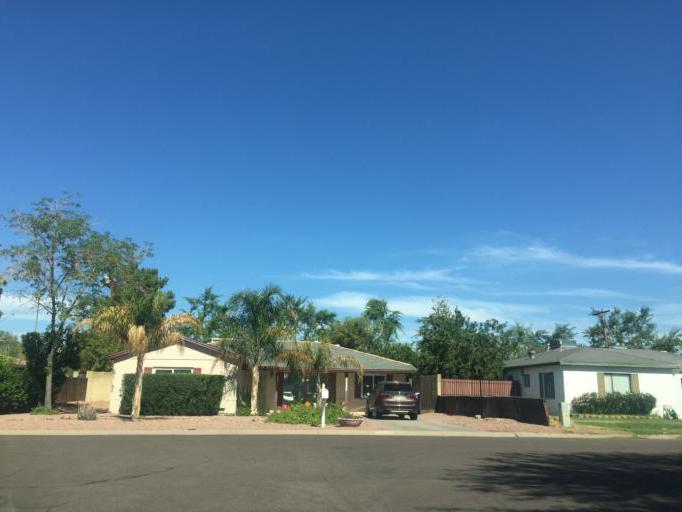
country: US
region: Arizona
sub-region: Maricopa County
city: Phoenix
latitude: 33.5396
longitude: -112.0572
